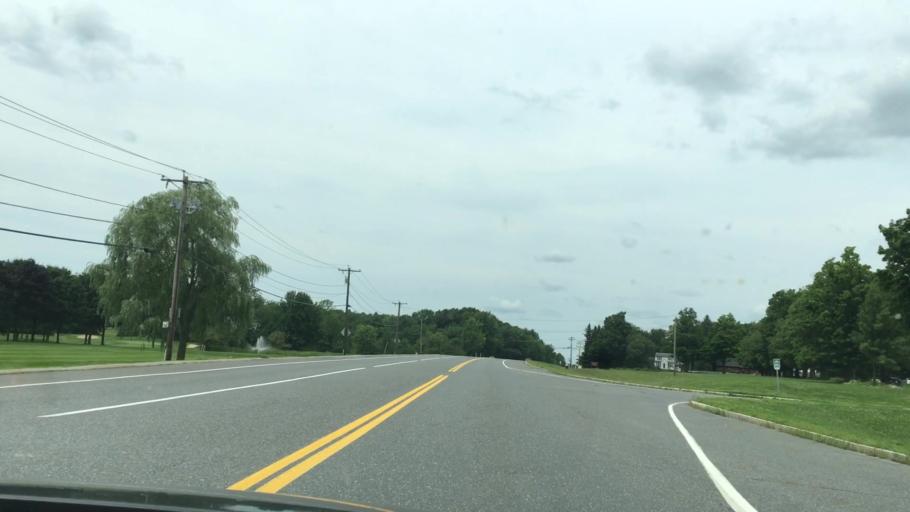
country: US
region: Massachusetts
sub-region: Worcester County
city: Gardner
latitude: 42.5953
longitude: -71.9875
